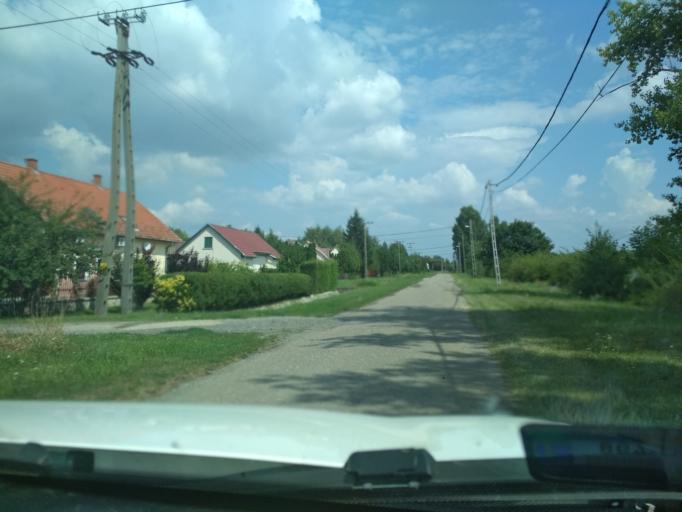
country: HU
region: Jasz-Nagykun-Szolnok
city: Abadszalok
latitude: 47.4686
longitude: 20.5798
